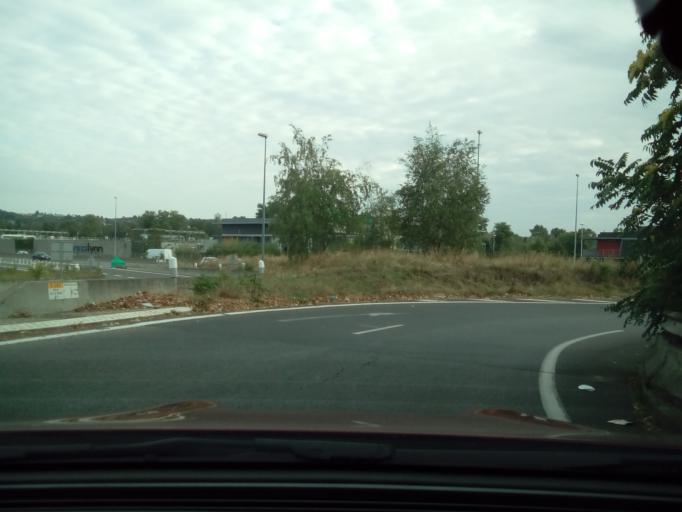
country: FR
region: Rhone-Alpes
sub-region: Departement du Rhone
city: Villeurbanne
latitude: 45.7872
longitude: 4.8865
